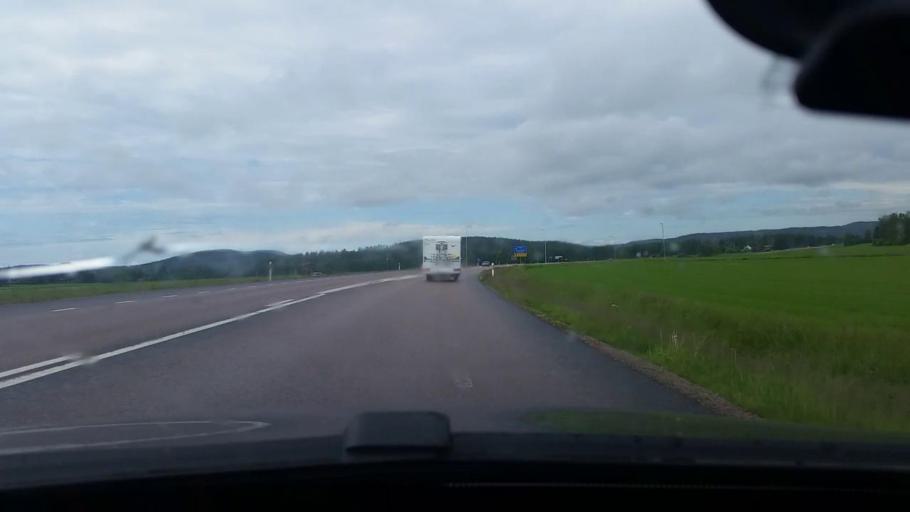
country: SE
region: Dalarna
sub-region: Gagnefs Kommun
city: Gagnef
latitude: 60.6033
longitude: 15.0560
